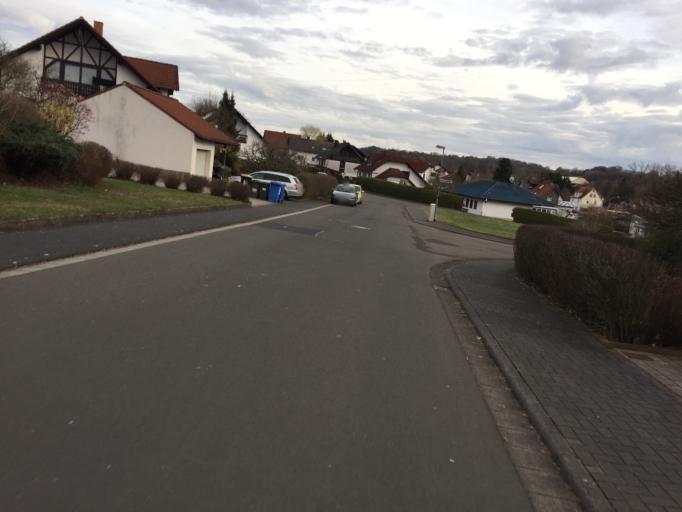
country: DE
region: Hesse
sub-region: Regierungsbezirk Giessen
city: Rabenau
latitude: 50.6732
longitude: 8.8702
